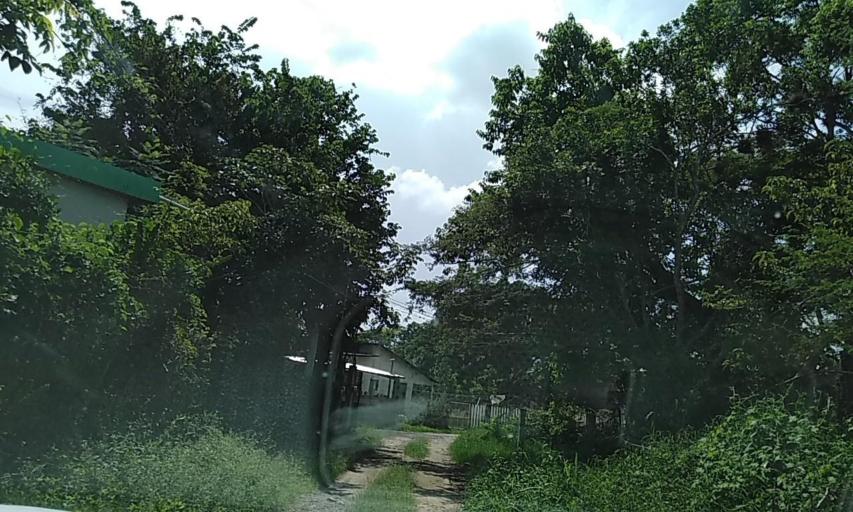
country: MX
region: Veracruz
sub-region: Emiliano Zapata
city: Dos Rios
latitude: 19.4430
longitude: -96.7824
